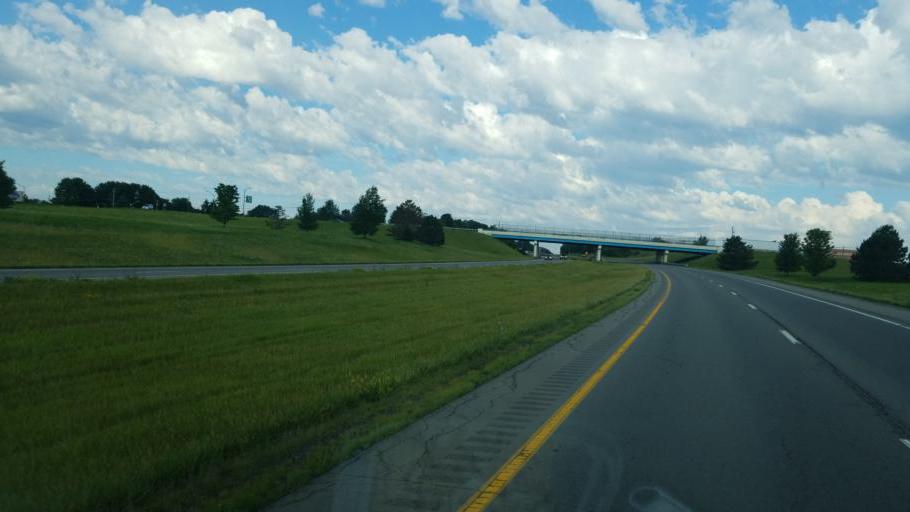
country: US
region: Ohio
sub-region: Richland County
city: Ontario
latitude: 40.7849
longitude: -82.5872
